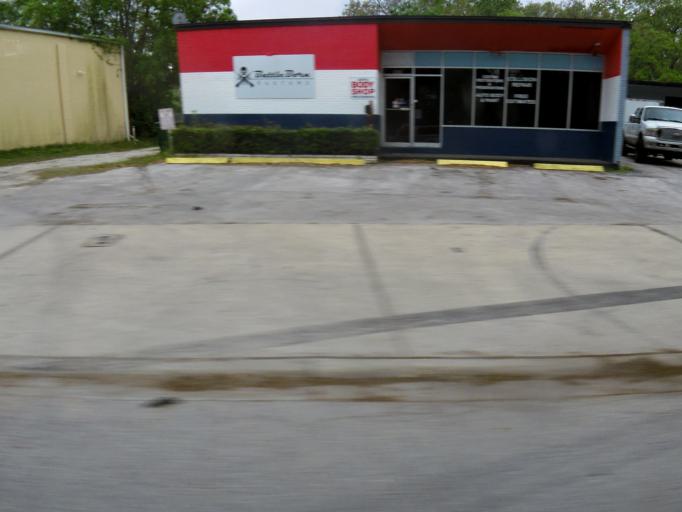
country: US
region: Florida
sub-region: Duval County
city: Jacksonville
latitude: 30.2898
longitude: -81.6254
